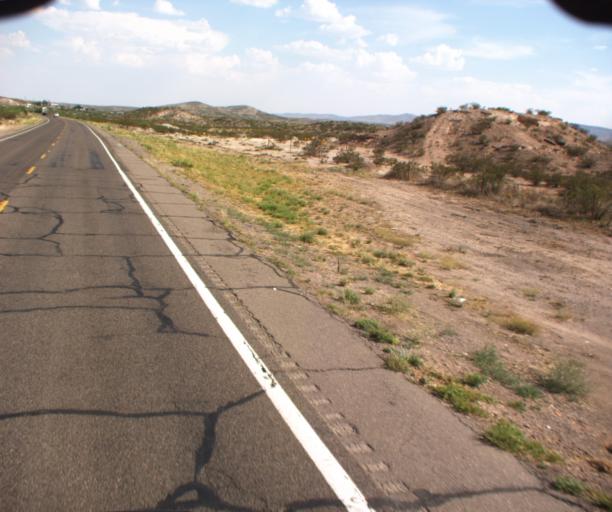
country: US
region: Arizona
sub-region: Greenlee County
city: Clifton
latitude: 32.7753
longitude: -109.1551
